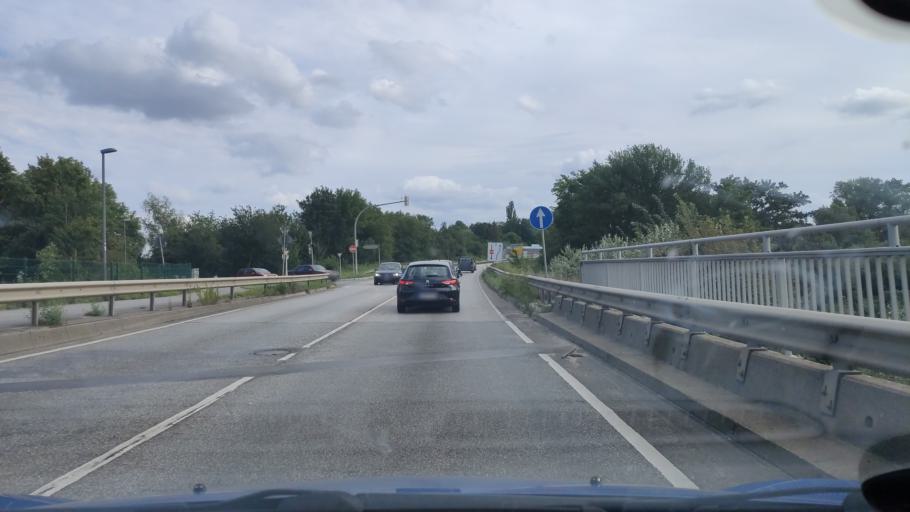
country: DE
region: Schleswig-Holstein
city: Kiel
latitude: 54.2897
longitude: 10.1312
